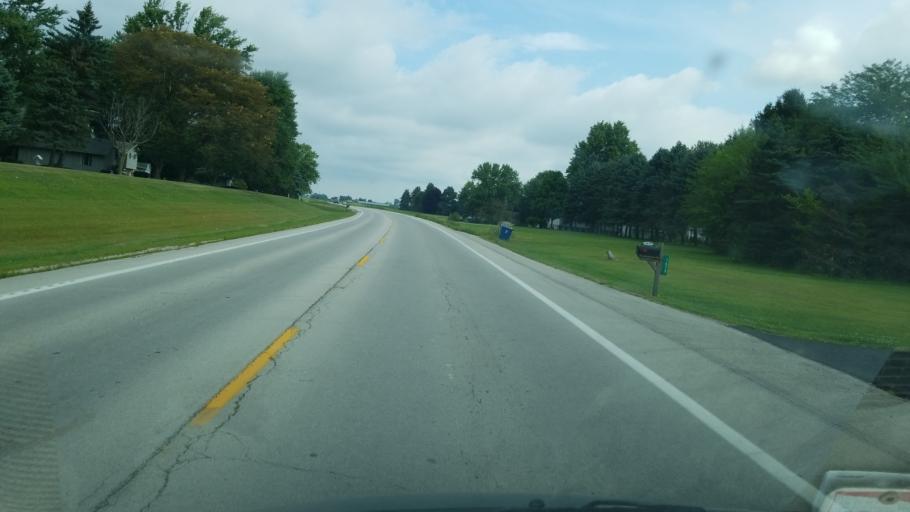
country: US
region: Ohio
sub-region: Sandusky County
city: Ballville
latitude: 41.2963
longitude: -83.1688
